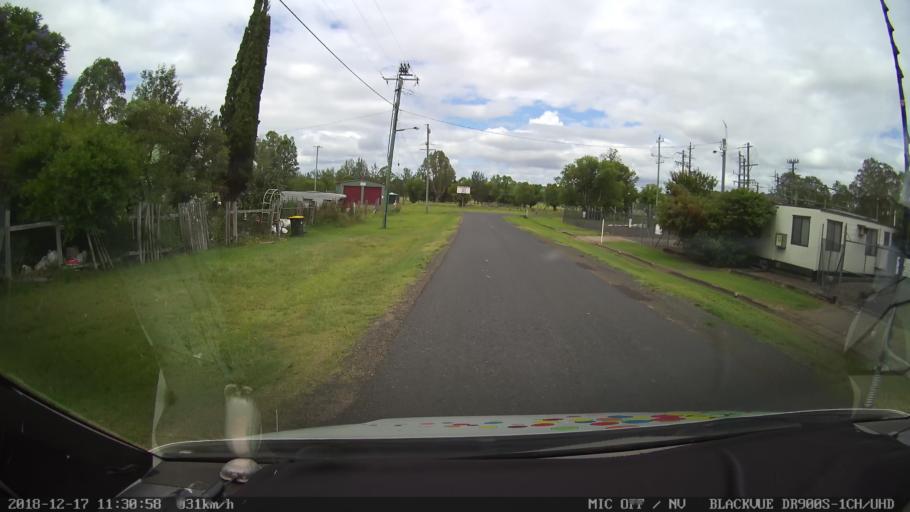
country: AU
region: New South Wales
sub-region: Kyogle
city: Kyogle
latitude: -28.7383
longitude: 152.6222
